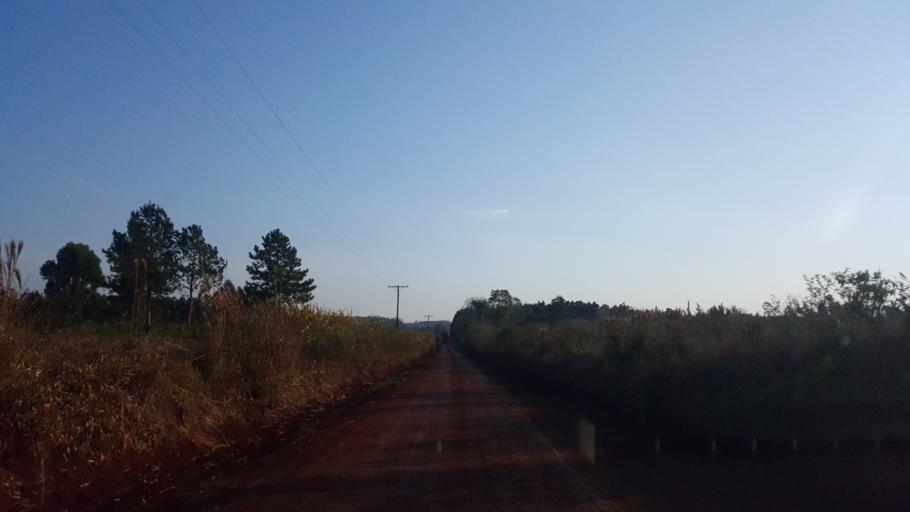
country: AR
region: Misiones
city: Capiovi
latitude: -26.9069
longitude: -55.0506
